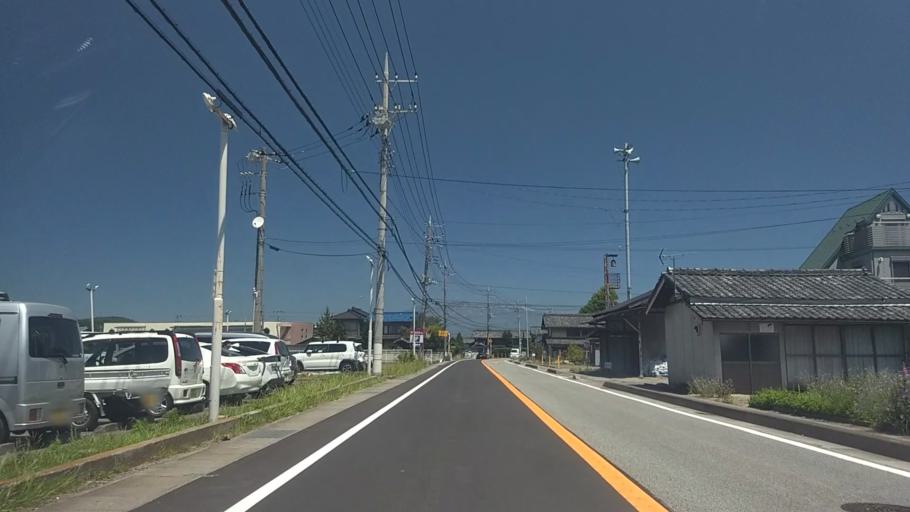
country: JP
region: Yamanashi
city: Nirasaki
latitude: 35.7247
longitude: 138.4497
